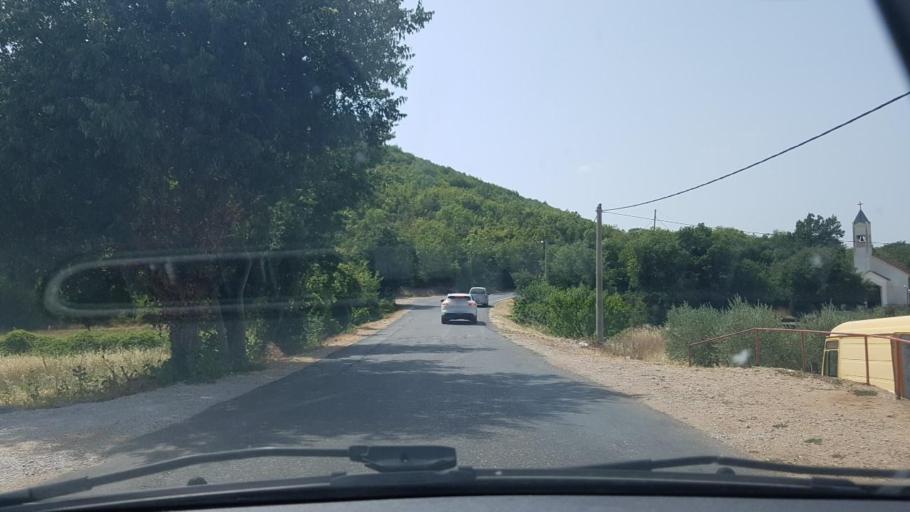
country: BA
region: Federation of Bosnia and Herzegovina
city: Tasovcici
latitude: 43.0342
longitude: 17.7276
